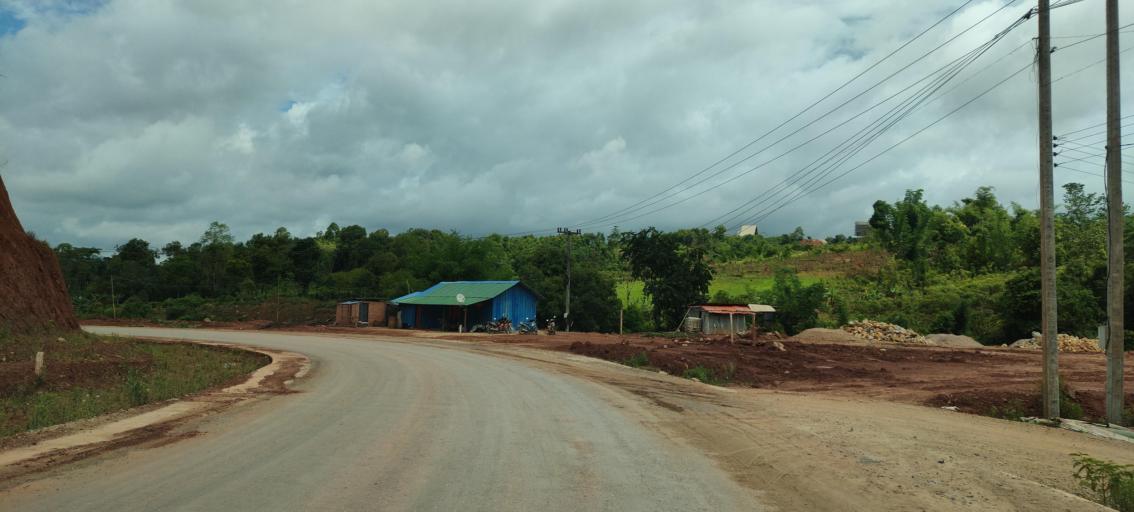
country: LA
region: Phongsali
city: Phongsali
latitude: 21.6375
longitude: 101.9193
